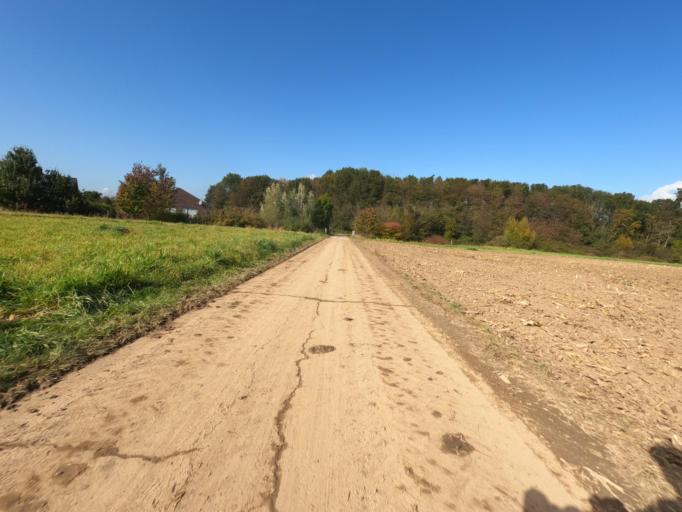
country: DE
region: North Rhine-Westphalia
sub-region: Regierungsbezirk Koln
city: Inden
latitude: 50.8729
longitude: 6.4050
